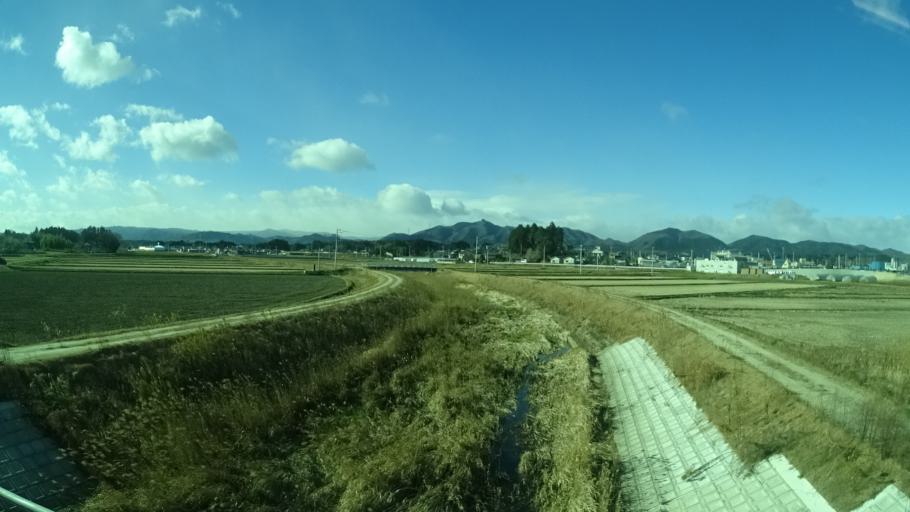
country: JP
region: Miyagi
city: Marumori
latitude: 37.8753
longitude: 140.9270
